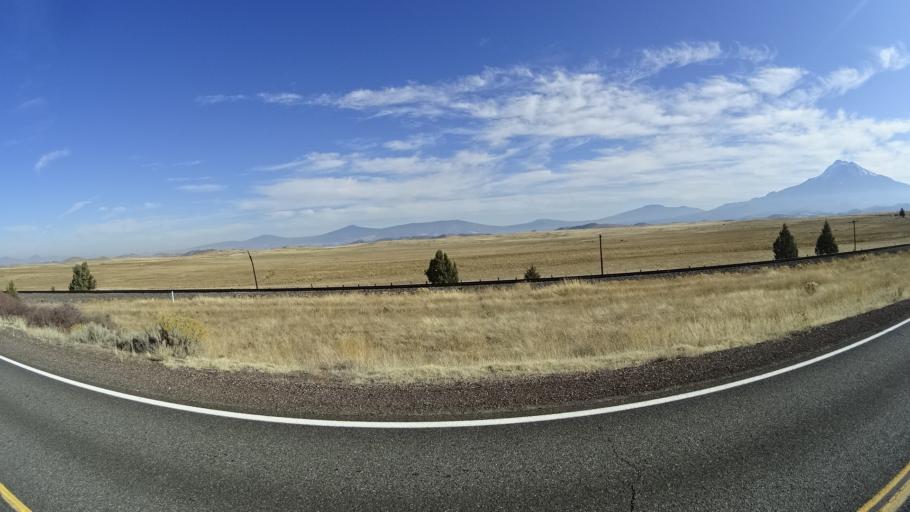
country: US
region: California
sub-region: Siskiyou County
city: Weed
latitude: 41.4949
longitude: -122.5109
